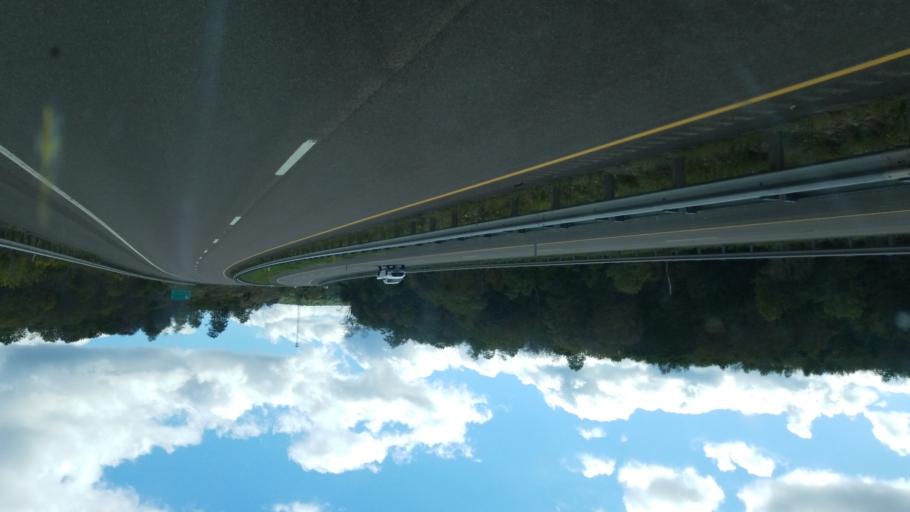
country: US
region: Pennsylvania
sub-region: Somerset County
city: Meyersdale
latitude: 39.6944
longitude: -79.1740
